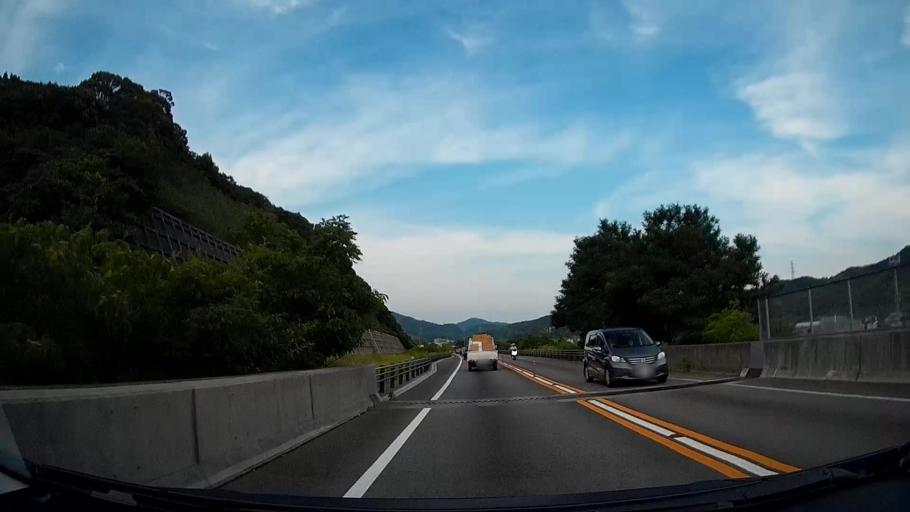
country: JP
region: Aichi
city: Gamagori
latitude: 34.8468
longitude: 137.1488
